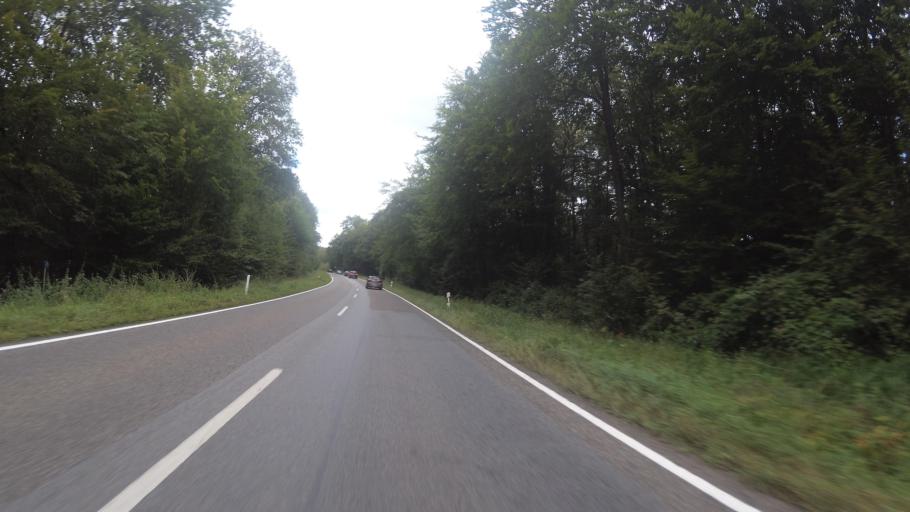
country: DE
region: Saarland
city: Riegelsberg
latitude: 49.2797
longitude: 6.9324
